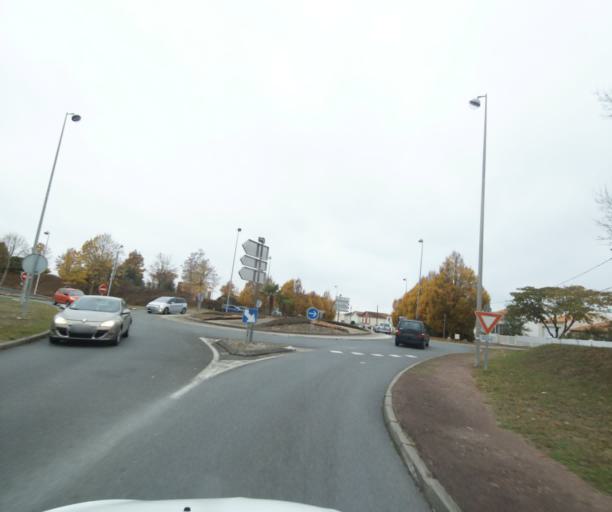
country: FR
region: Poitou-Charentes
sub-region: Departement de la Charente-Maritime
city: Les Gonds
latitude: 45.7343
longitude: -0.6111
